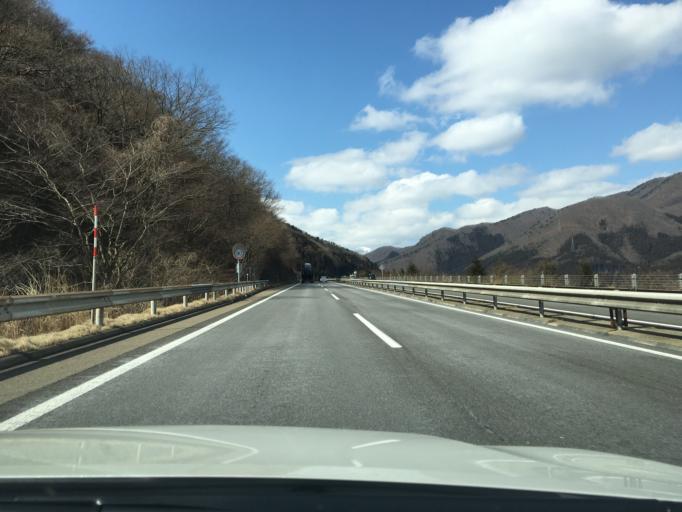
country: JP
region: Miyagi
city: Shiroishi
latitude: 38.1976
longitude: 140.5884
